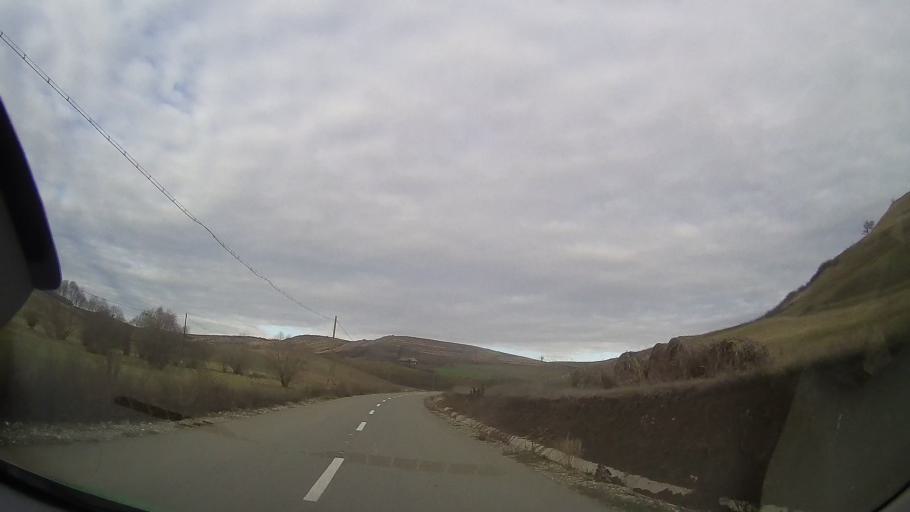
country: RO
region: Bistrita-Nasaud
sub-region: Comuna Silvasu de Campie
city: Silvasu de Campie
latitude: 46.8171
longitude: 24.2971
